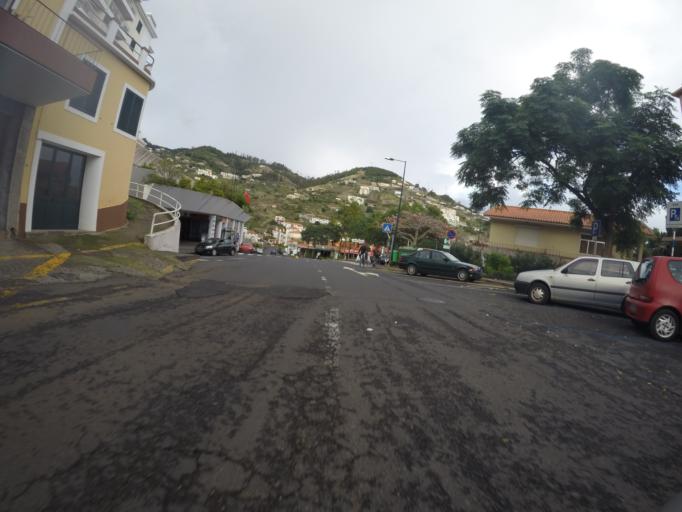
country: PT
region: Madeira
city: Canico
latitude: 32.6529
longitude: -16.8419
